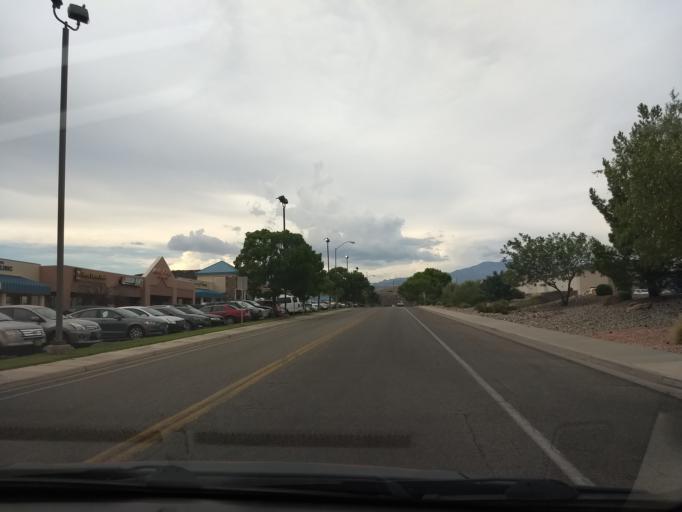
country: US
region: Utah
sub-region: Washington County
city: Saint George
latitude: 37.1147
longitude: -113.5476
